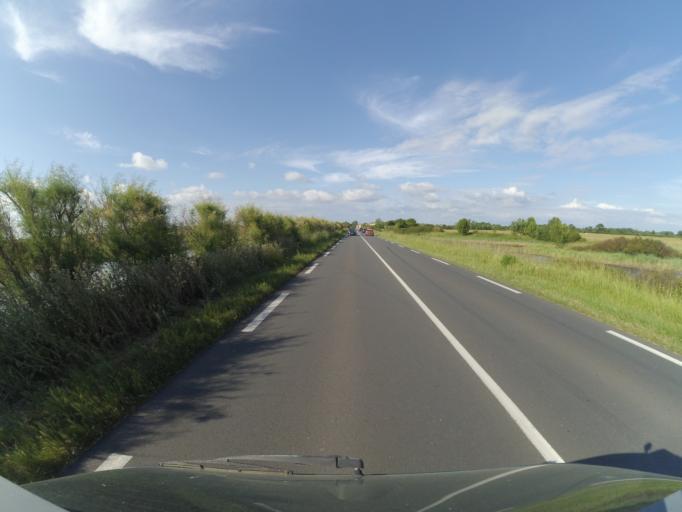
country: FR
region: Poitou-Charentes
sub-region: Departement de la Charente-Maritime
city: Le Gua
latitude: 45.7214
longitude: -0.9666
